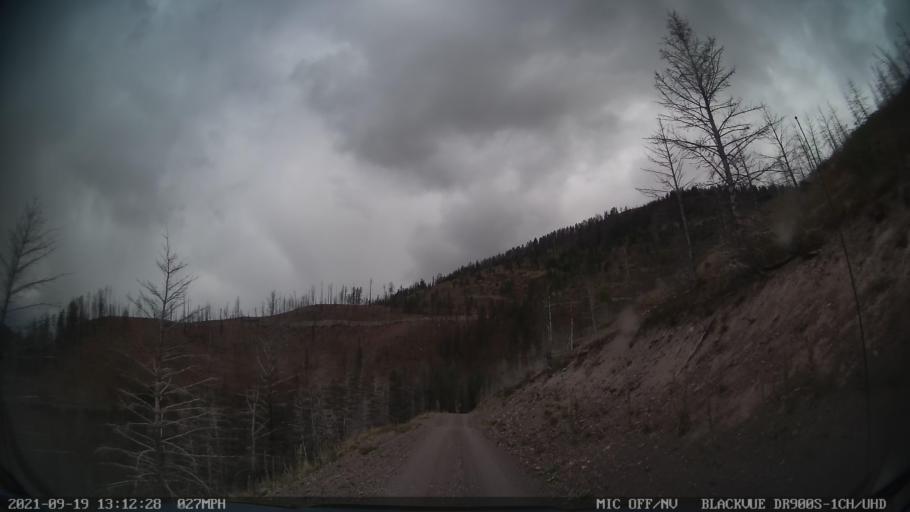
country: US
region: Montana
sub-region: Missoula County
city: Seeley Lake
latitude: 47.1763
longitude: -113.3549
